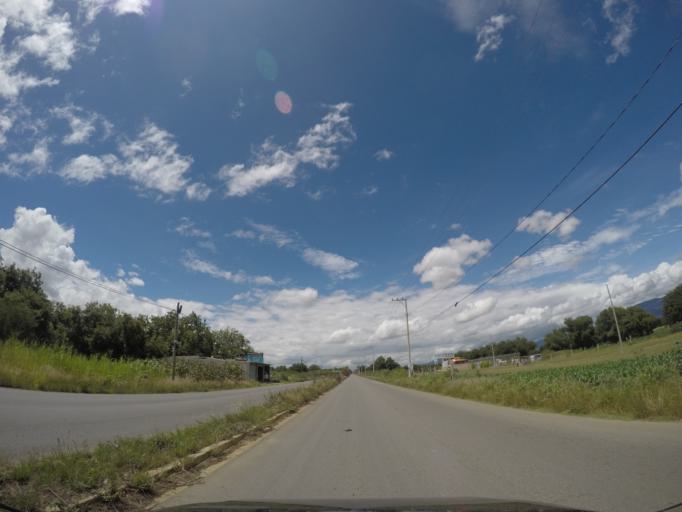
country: MX
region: Oaxaca
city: San Raymundo Jalpam
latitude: 16.9802
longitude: -96.7489
